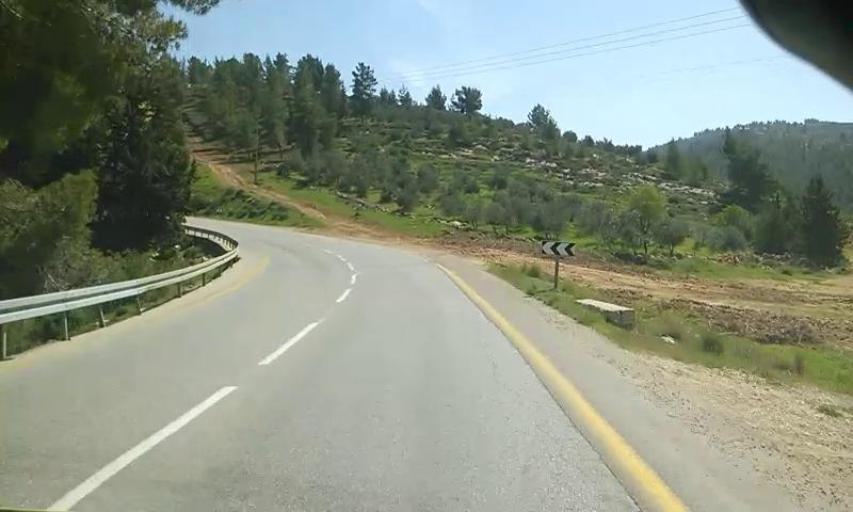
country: PS
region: West Bank
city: Nahhalin
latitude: 31.6738
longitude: 35.1009
